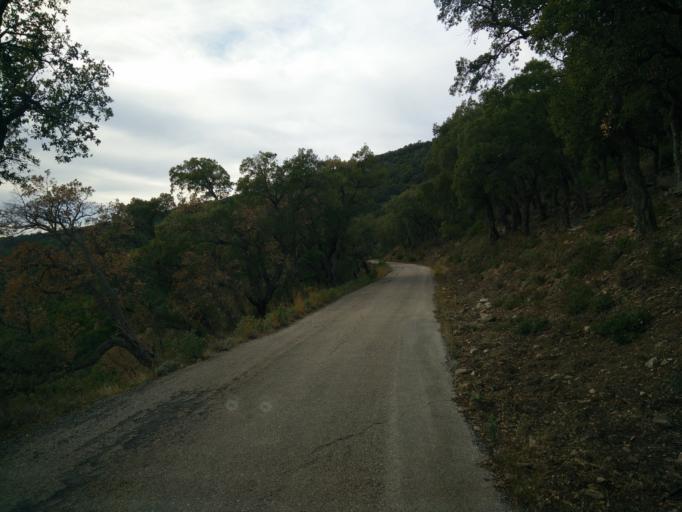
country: FR
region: Provence-Alpes-Cote d'Azur
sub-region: Departement du Var
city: Roquebrune-sur-Argens
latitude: 43.3979
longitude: 6.6185
